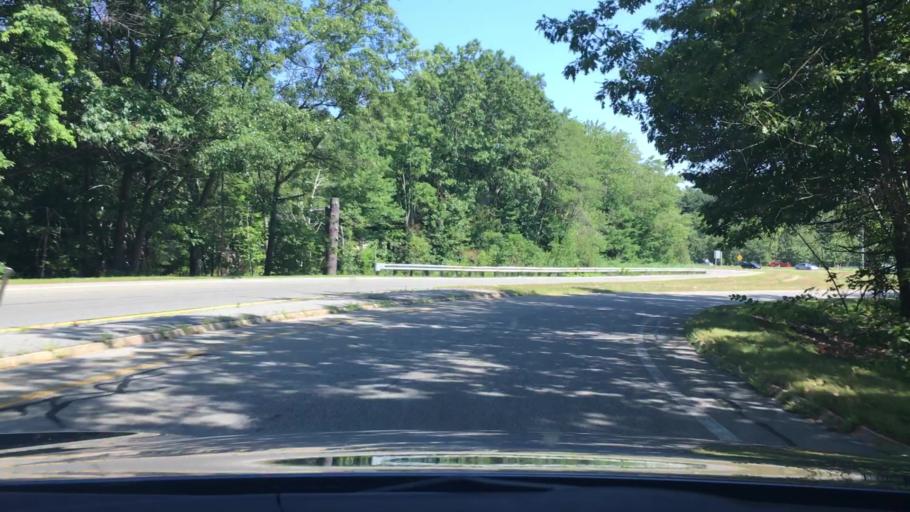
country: US
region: Massachusetts
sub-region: Middlesex County
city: Billerica
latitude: 42.5609
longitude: -71.2999
